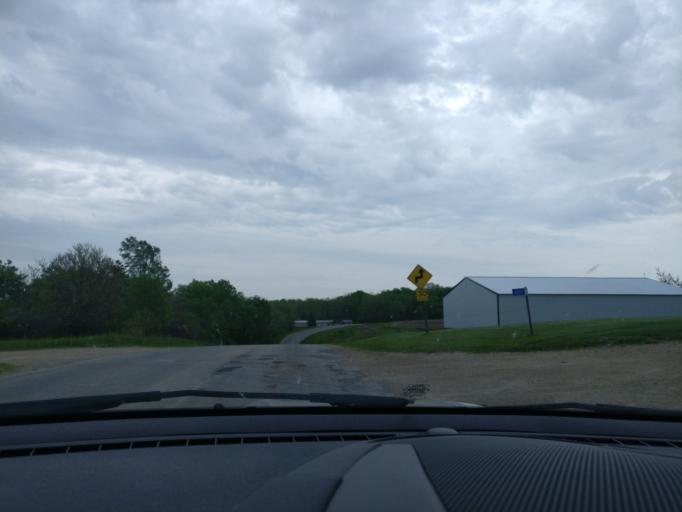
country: US
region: Wisconsin
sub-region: Lafayette County
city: Darlington
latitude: 42.7514
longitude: -89.9925
